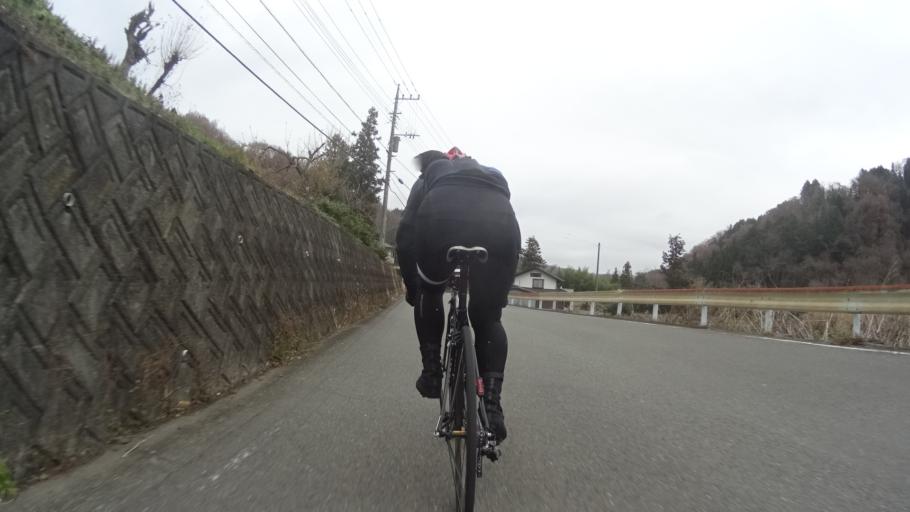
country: JP
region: Yamanashi
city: Uenohara
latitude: 35.6374
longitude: 139.0871
